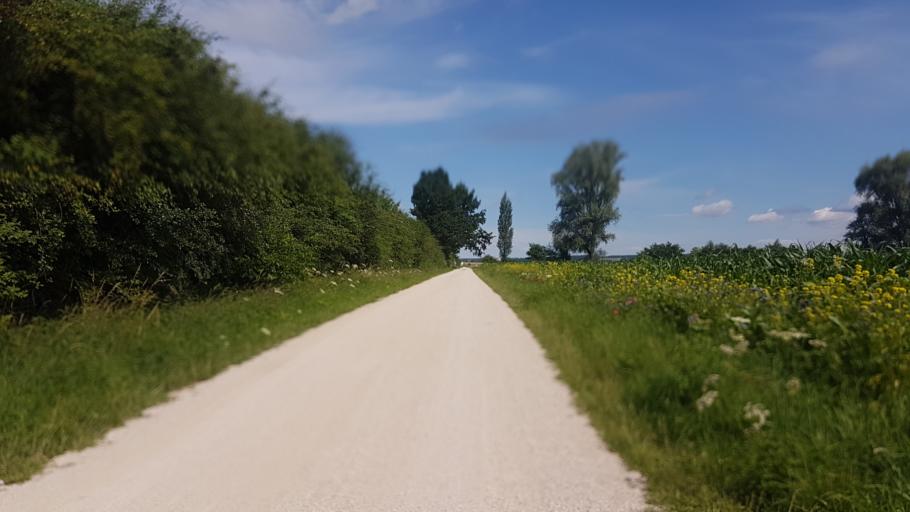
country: DE
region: Bavaria
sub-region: Regierungsbezirk Mittelfranken
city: Markt Berolzheim
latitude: 49.0180
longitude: 10.8525
